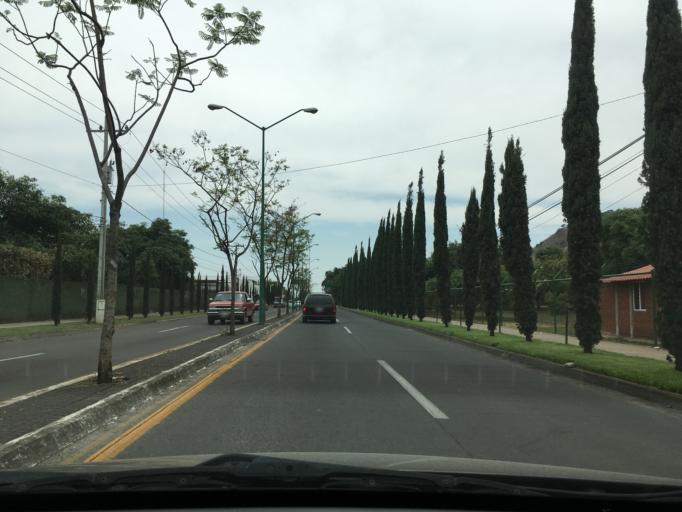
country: MX
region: Michoacan
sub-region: Uruapan
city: Uruapan
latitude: 19.3978
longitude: -102.0686
